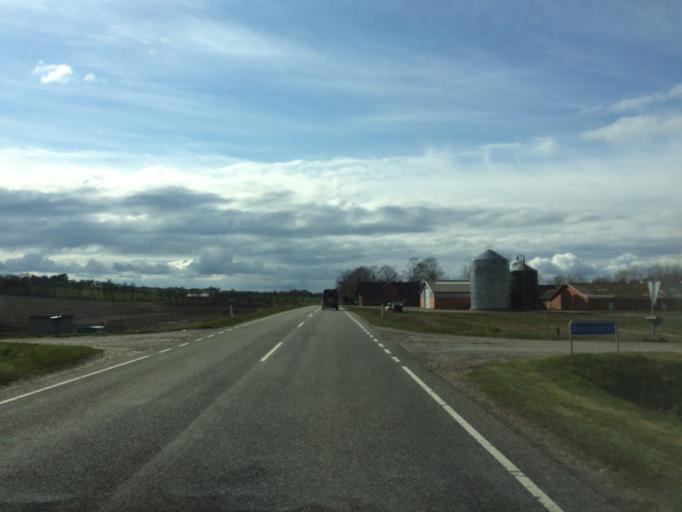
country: DK
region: Central Jutland
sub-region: Herning Kommune
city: Vildbjerg
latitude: 56.1806
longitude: 8.7216
